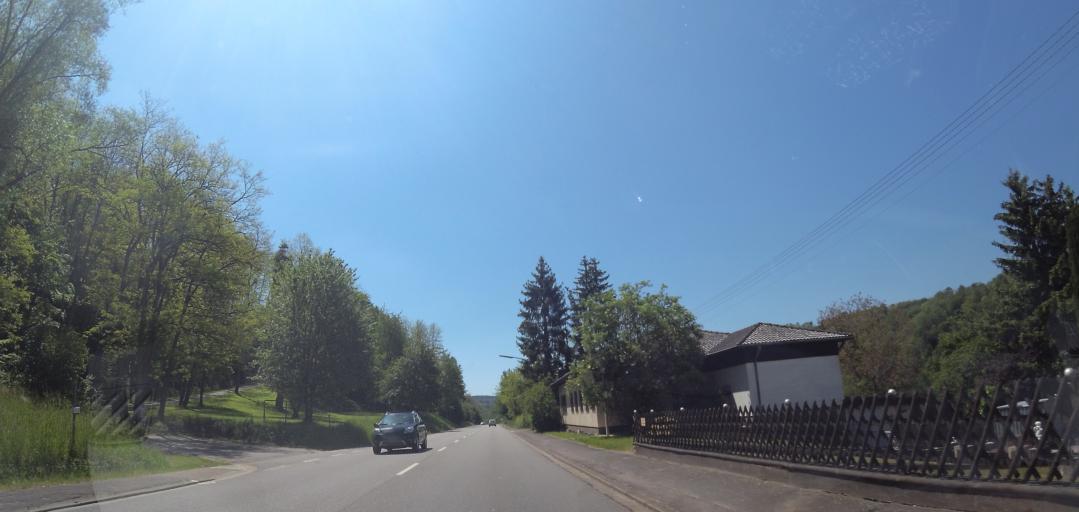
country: DE
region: Saarland
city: Merzig
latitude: 49.4619
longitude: 6.6783
